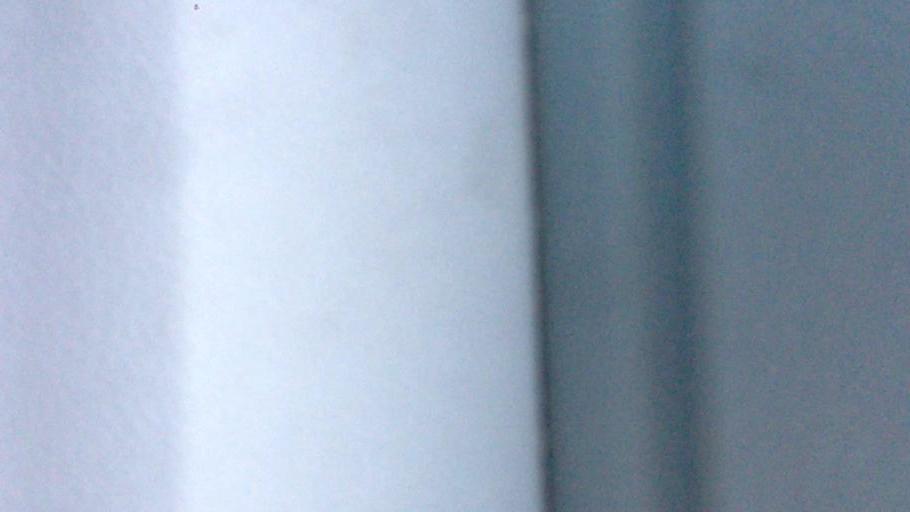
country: US
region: New York
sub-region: Dutchess County
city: Rhinebeck
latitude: 41.9699
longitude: -73.9210
